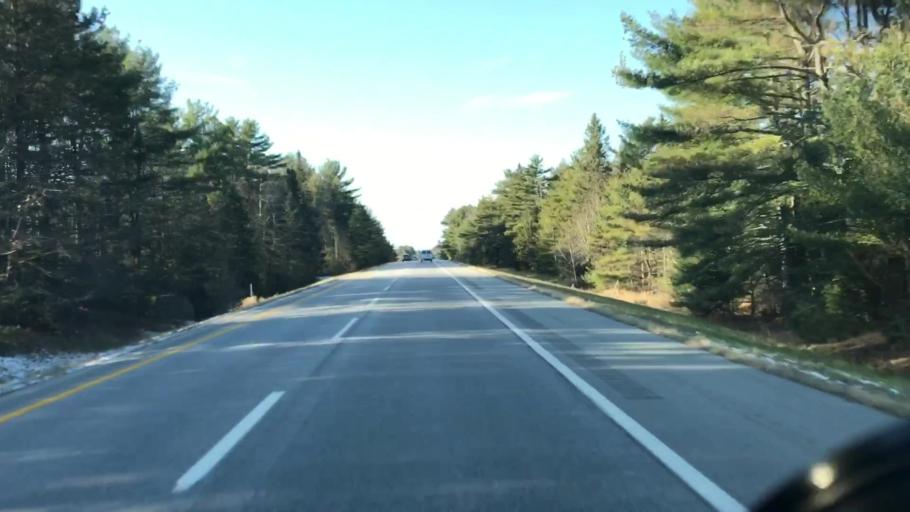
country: US
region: Maine
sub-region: Penobscot County
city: Plymouth
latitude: 44.7959
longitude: -69.2101
